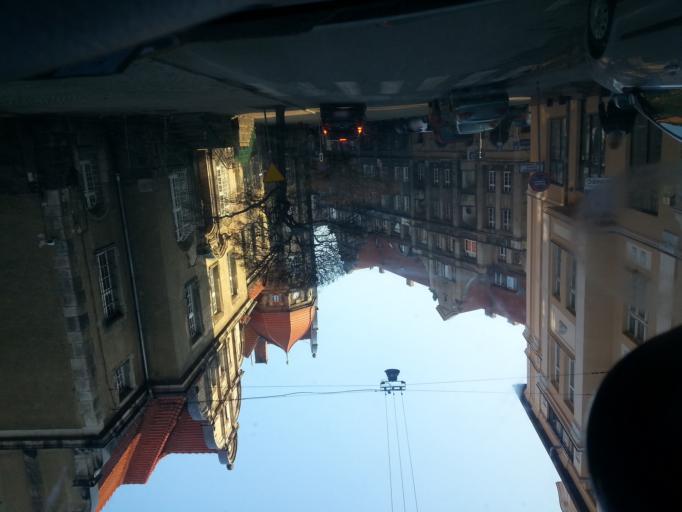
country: PL
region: Lower Silesian Voivodeship
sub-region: Jelenia Gora
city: Jelenia Gora
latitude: 50.9019
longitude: 15.7412
